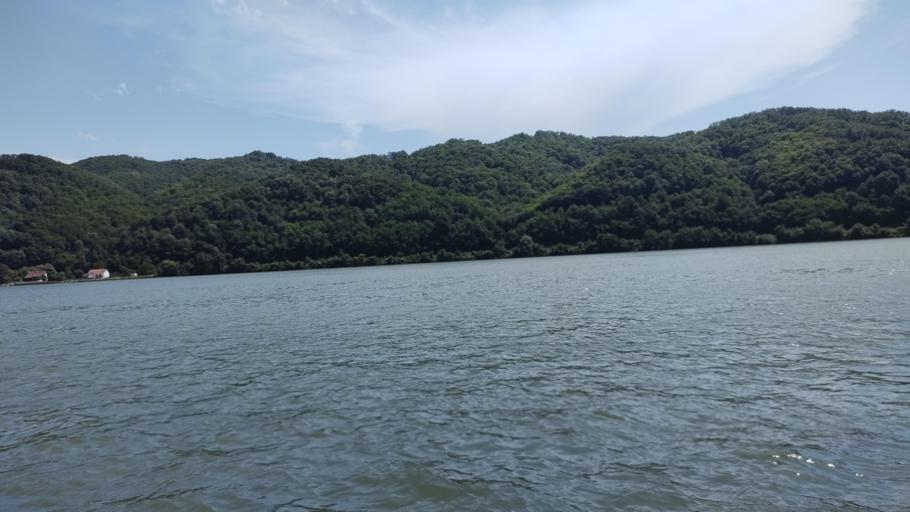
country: RS
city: Radenka
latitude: 44.6600
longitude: 21.7830
